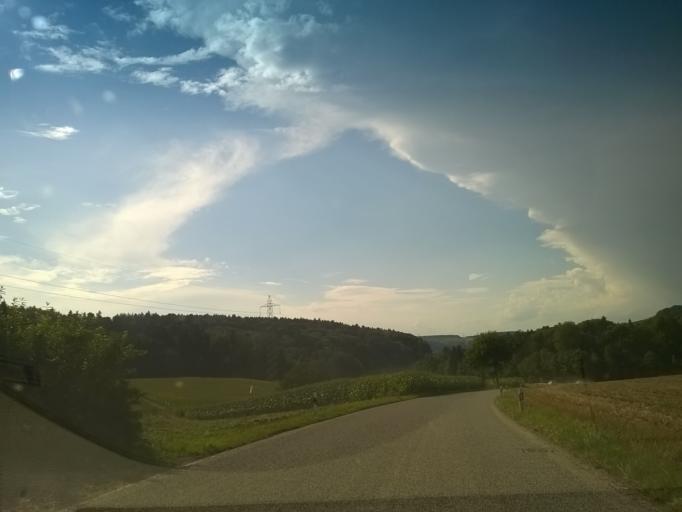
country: CH
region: Zurich
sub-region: Bezirk Buelach
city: Birchwil
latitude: 47.4800
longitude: 8.6414
